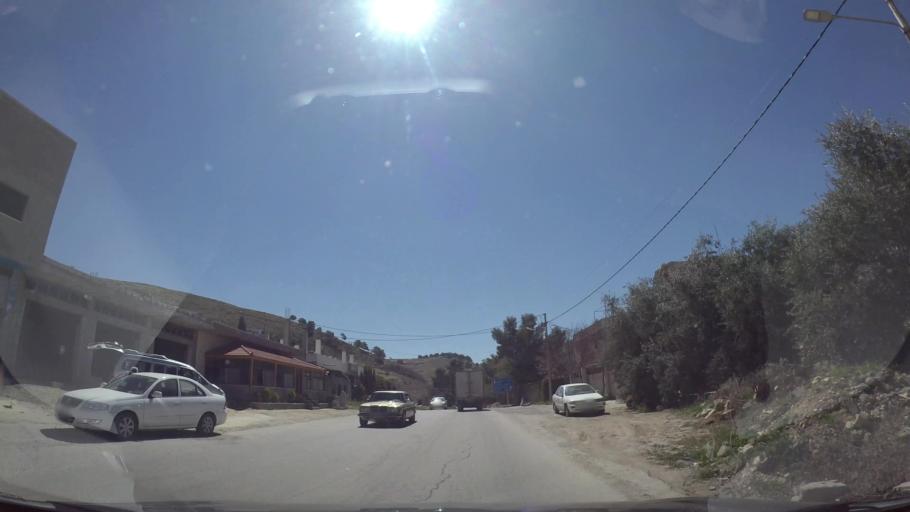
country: JO
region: Tafielah
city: At Tafilah
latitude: 30.8204
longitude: 35.5867
